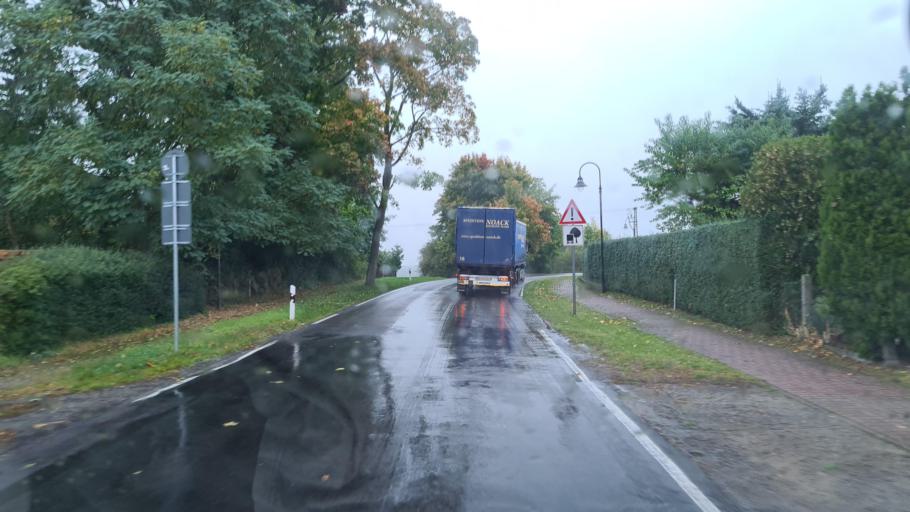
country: DE
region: Brandenburg
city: Rietz Neuendorf
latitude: 52.2600
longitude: 14.1572
